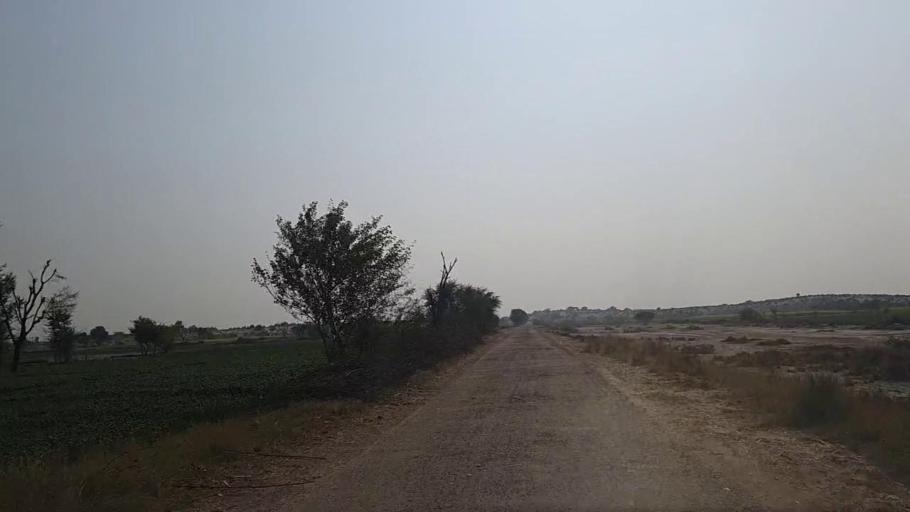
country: PK
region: Sindh
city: Jam Sahib
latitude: 26.4511
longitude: 68.5234
